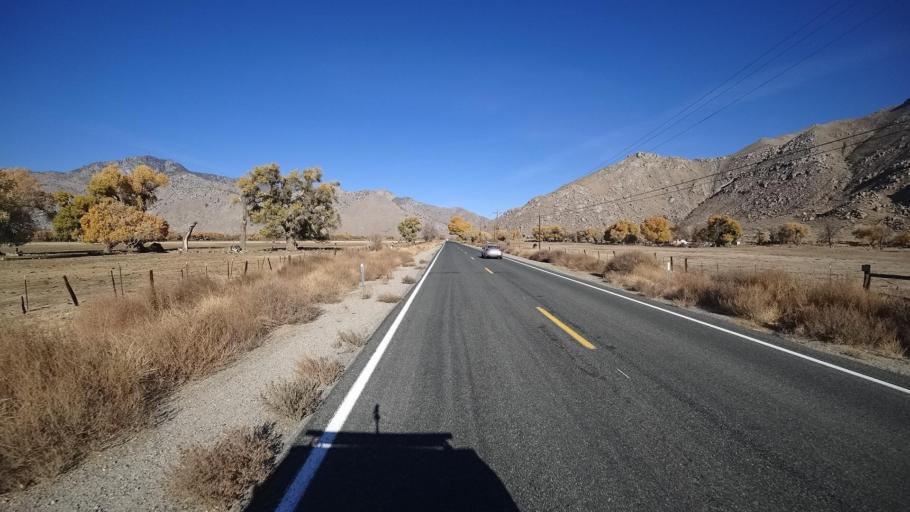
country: US
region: California
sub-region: Kern County
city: Weldon
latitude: 35.6725
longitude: -118.2597
